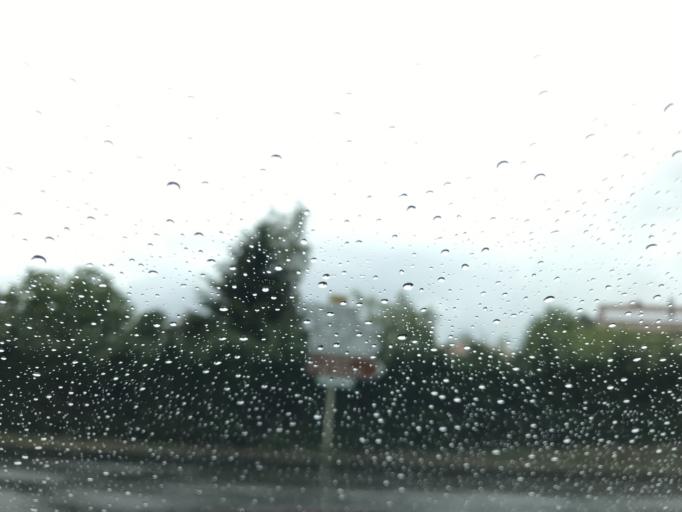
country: FR
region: Auvergne
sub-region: Departement du Puy-de-Dome
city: Montaigut
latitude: 45.6961
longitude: 3.4310
